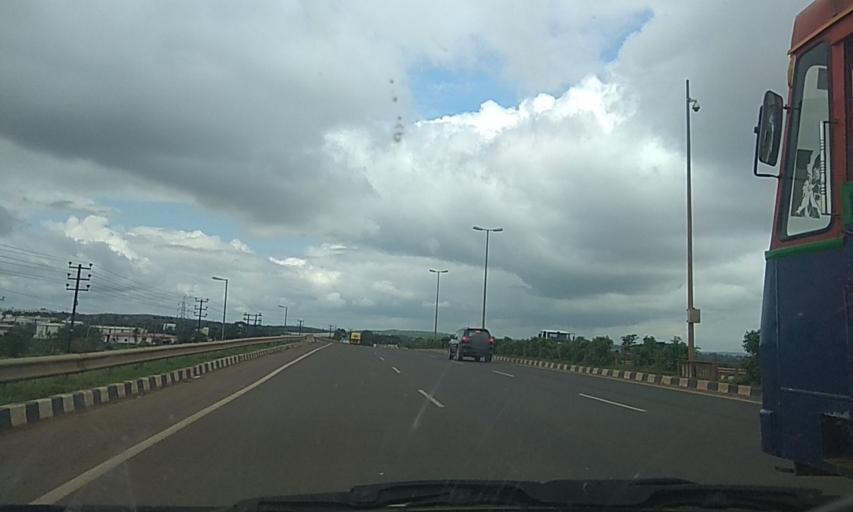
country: IN
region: Karnataka
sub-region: Dharwad
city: Alnavar
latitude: 15.5167
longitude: 74.9260
